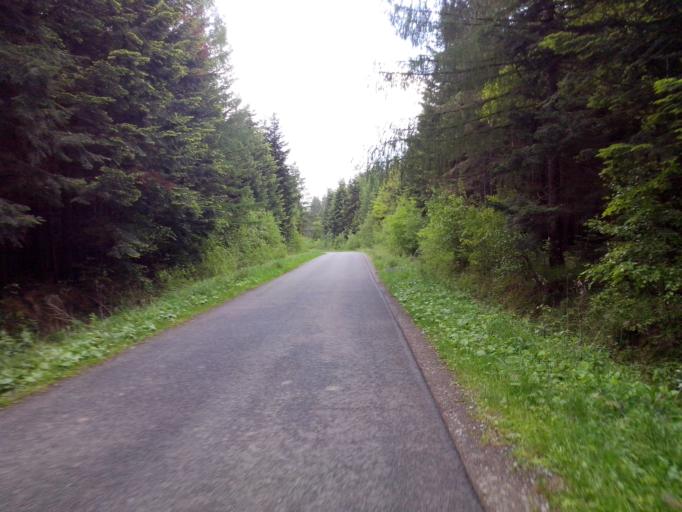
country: PL
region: Subcarpathian Voivodeship
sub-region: Powiat strzyzowski
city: Wysoka Strzyzowska
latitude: 49.8177
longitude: 21.7885
